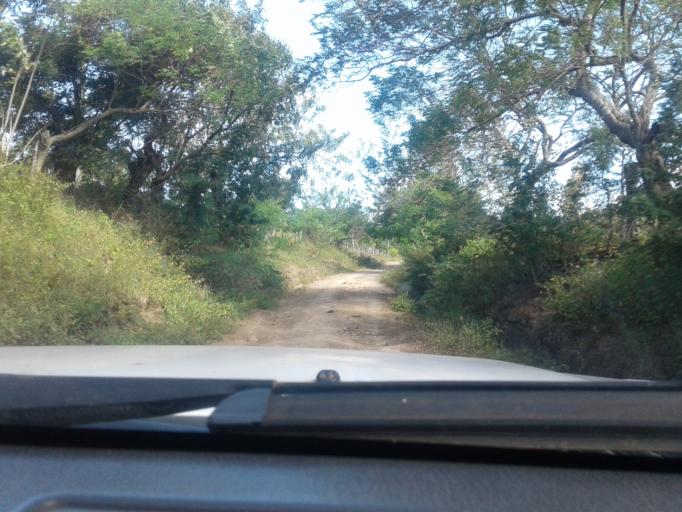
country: NI
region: Carazo
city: Santa Teresa
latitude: 11.7634
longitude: -86.1791
